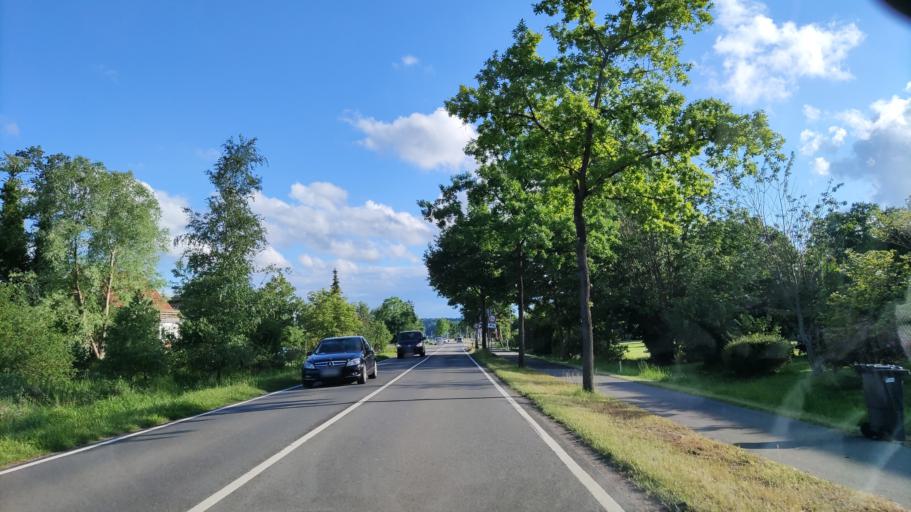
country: DE
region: Lower Saxony
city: Buxtehude
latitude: 53.4946
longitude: 9.6541
